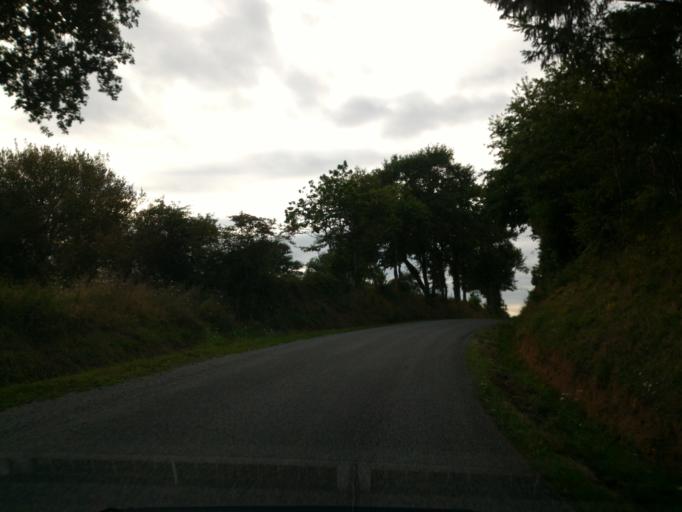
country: FR
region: Poitou-Charentes
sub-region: Departement de la Charente
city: Brigueuil
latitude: 45.9148
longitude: 0.8515
